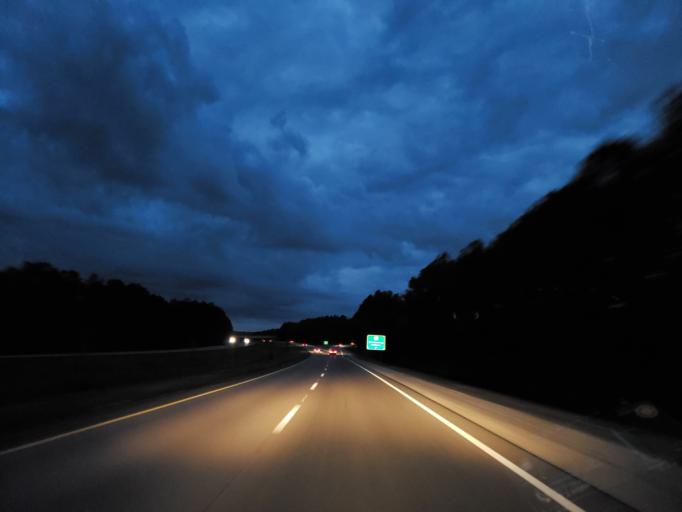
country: US
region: Mississippi
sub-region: Forrest County
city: Hattiesburg
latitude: 31.2463
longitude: -89.2678
